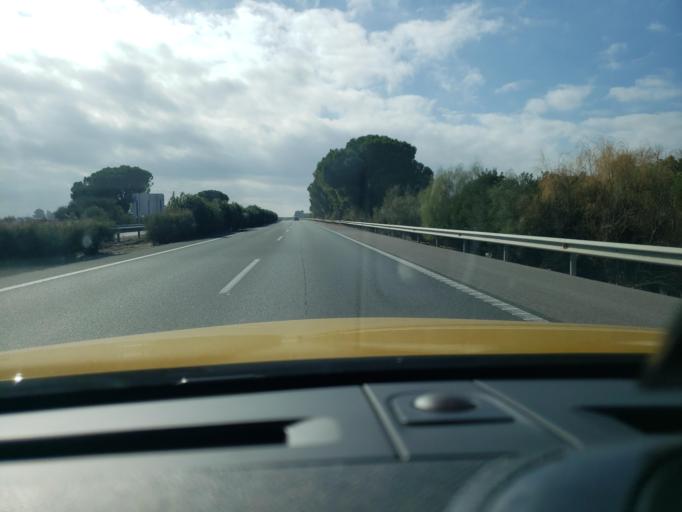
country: ES
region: Andalusia
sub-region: Provincia de Sevilla
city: Los Palacios y Villafranca
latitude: 37.1520
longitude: -5.9135
